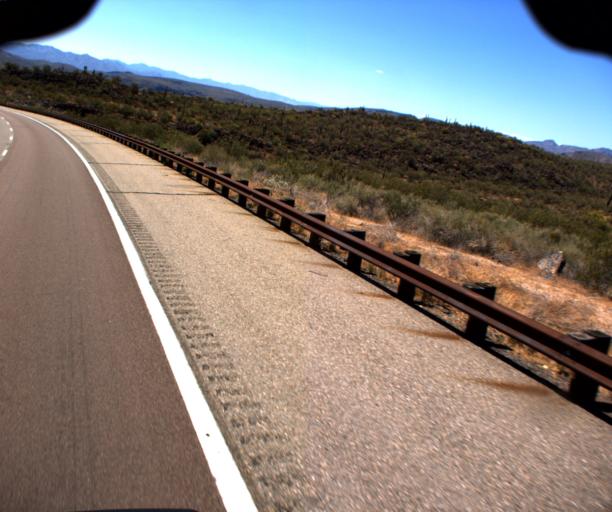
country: US
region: Arizona
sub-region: Yavapai County
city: Bagdad
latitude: 34.5012
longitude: -113.3993
